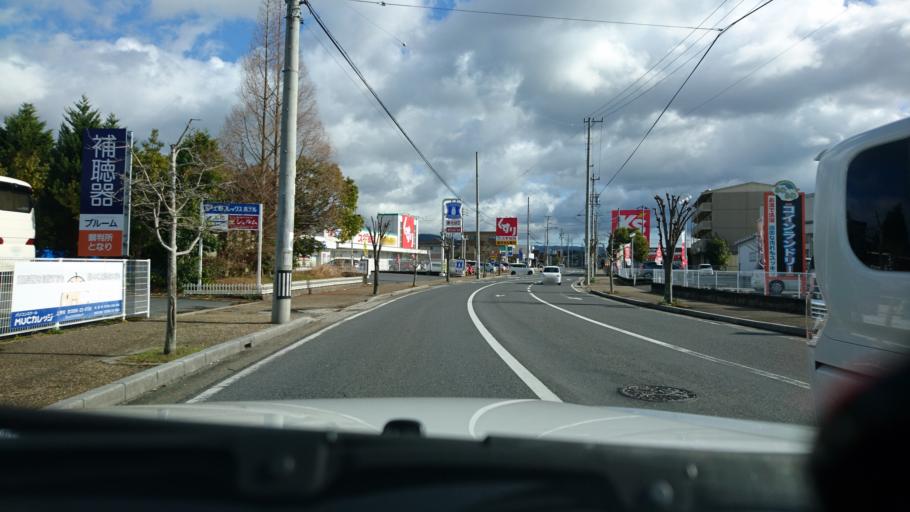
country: JP
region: Mie
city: Ueno-ebisumachi
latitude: 34.7747
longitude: 136.1301
